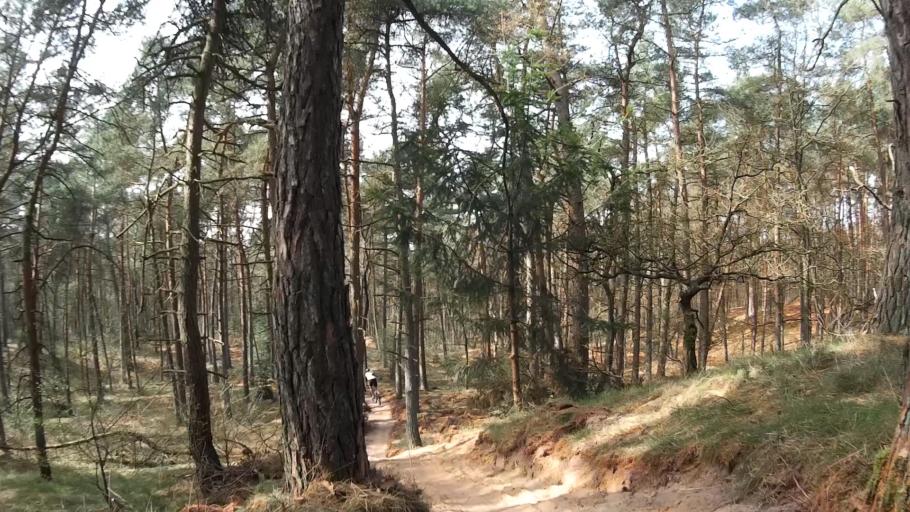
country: NL
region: Utrecht
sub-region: Gemeente Utrechtse Heuvelrug
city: Driebergen-Rijsenburg
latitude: 52.0682
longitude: 5.2974
